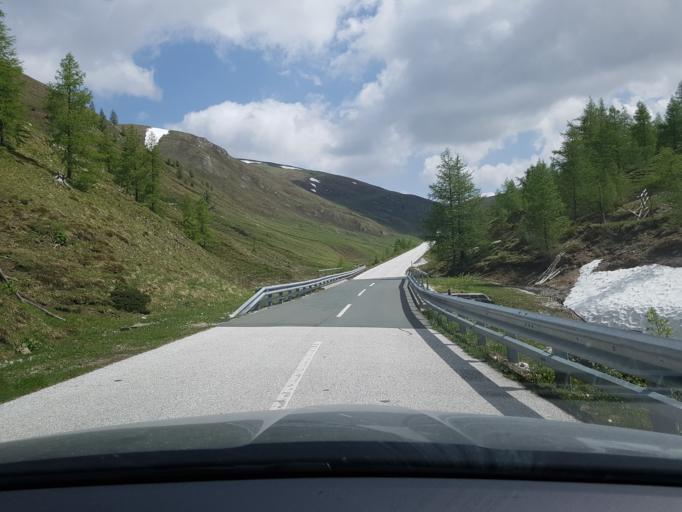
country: AT
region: Salzburg
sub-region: Politischer Bezirk Tamsweg
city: Thomatal
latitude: 46.9437
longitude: 13.7449
